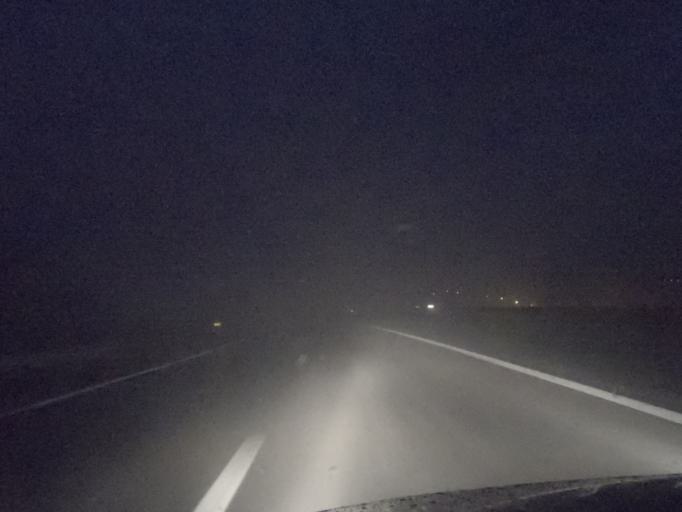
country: PT
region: Vila Real
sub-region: Santa Marta de Penaguiao
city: Santa Marta de Penaguiao
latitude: 41.2212
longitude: -7.7352
